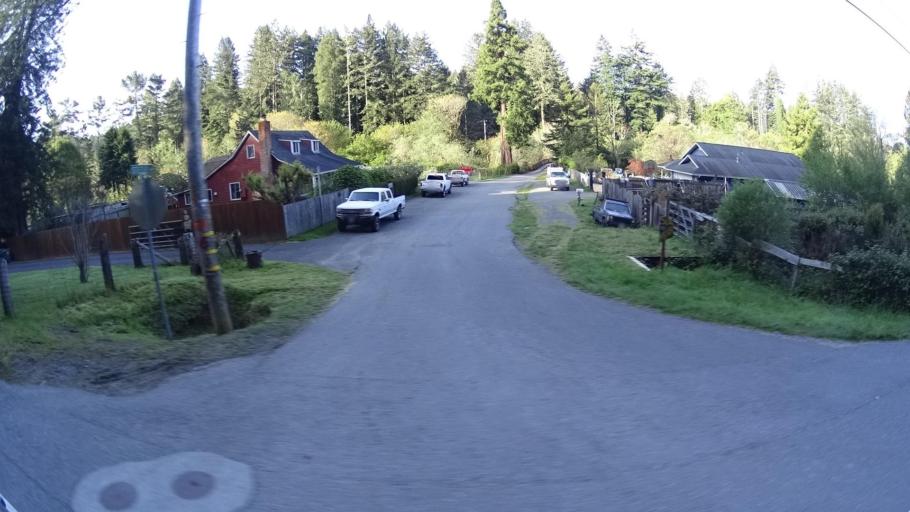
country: US
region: California
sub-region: Humboldt County
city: Bayside
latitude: 40.7590
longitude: -124.0511
